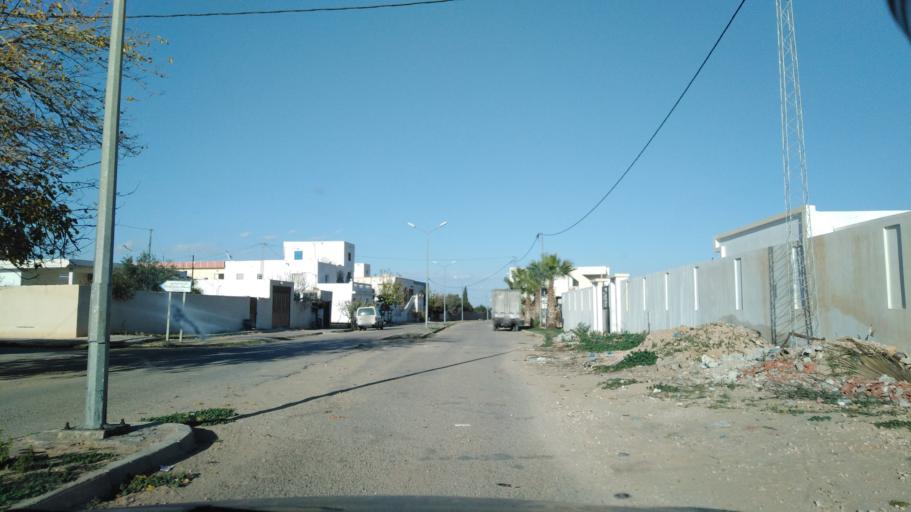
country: TN
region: Al Mahdiyah
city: Shurban
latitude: 34.9624
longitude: 10.3685
